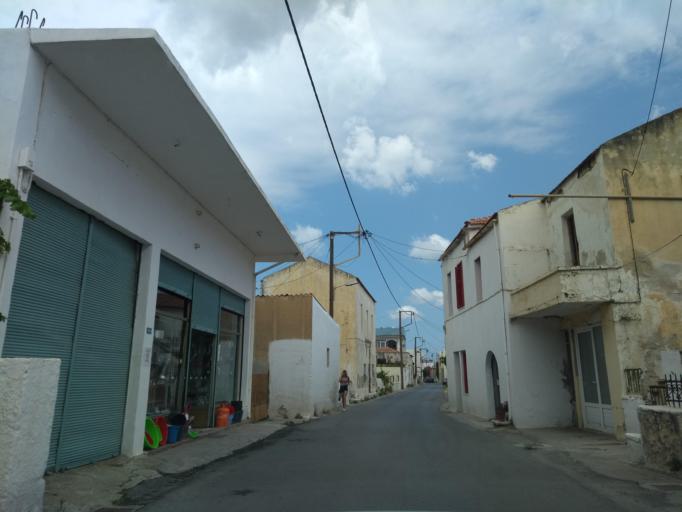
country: GR
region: Crete
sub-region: Nomos Chanias
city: Kalivai
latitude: 35.4548
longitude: 24.1704
